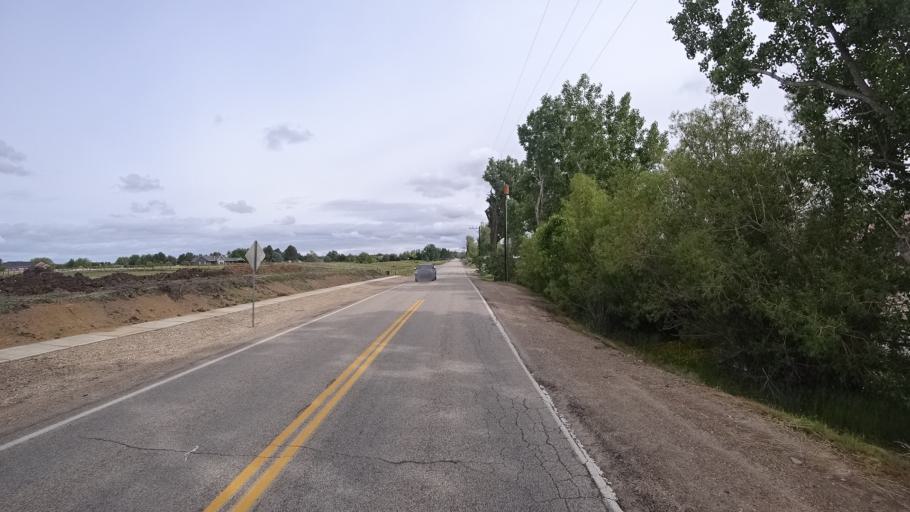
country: US
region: Idaho
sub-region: Ada County
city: Eagle
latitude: 43.7221
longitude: -116.3542
